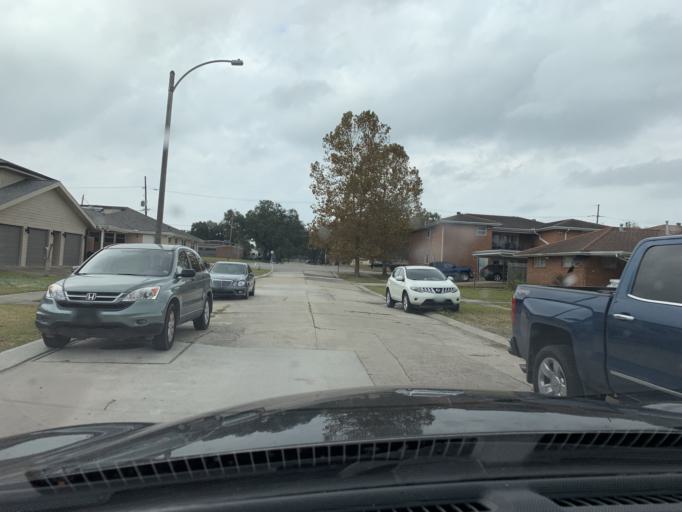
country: US
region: Louisiana
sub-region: Jefferson Parish
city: Metairie
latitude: 30.0182
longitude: -90.0999
